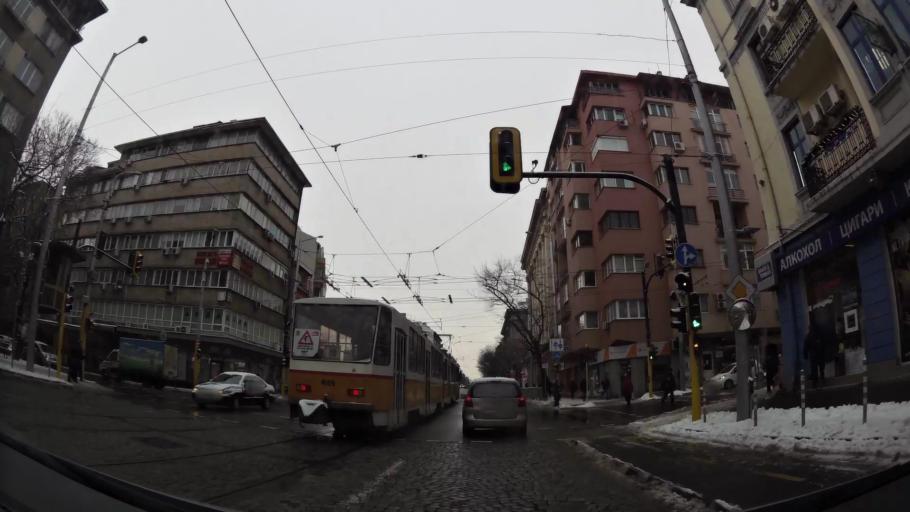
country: BG
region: Sofia-Capital
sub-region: Stolichna Obshtina
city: Sofia
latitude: 42.6981
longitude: 23.3296
